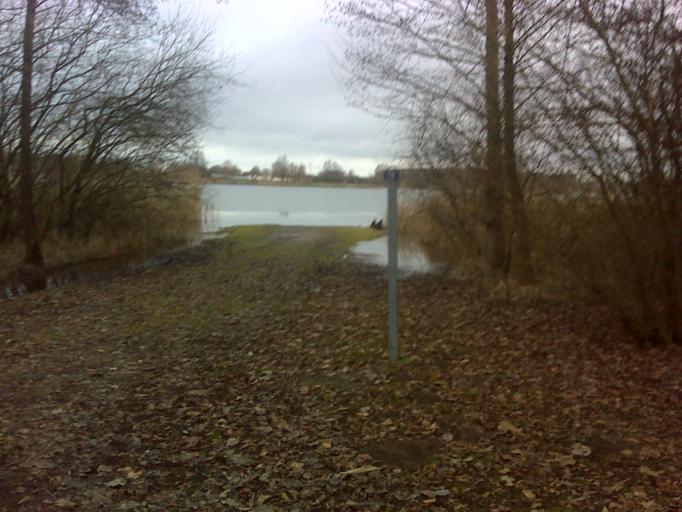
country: FR
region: Lorraine
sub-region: Departement de la Moselle
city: Morhange
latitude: 48.9497
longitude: 6.6455
